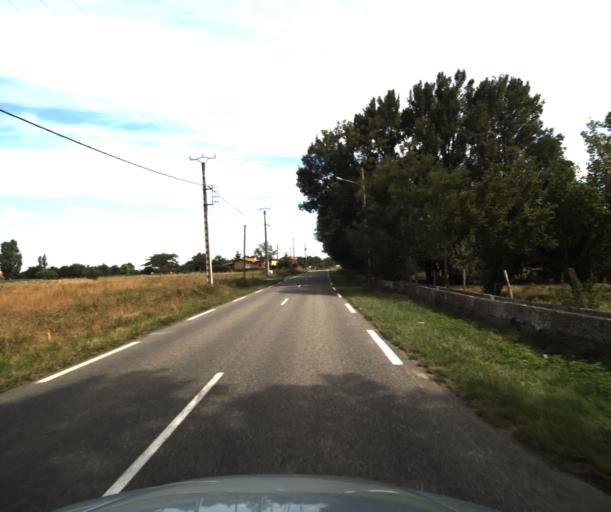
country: FR
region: Midi-Pyrenees
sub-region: Departement de la Haute-Garonne
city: Seysses
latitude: 43.4772
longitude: 1.3041
